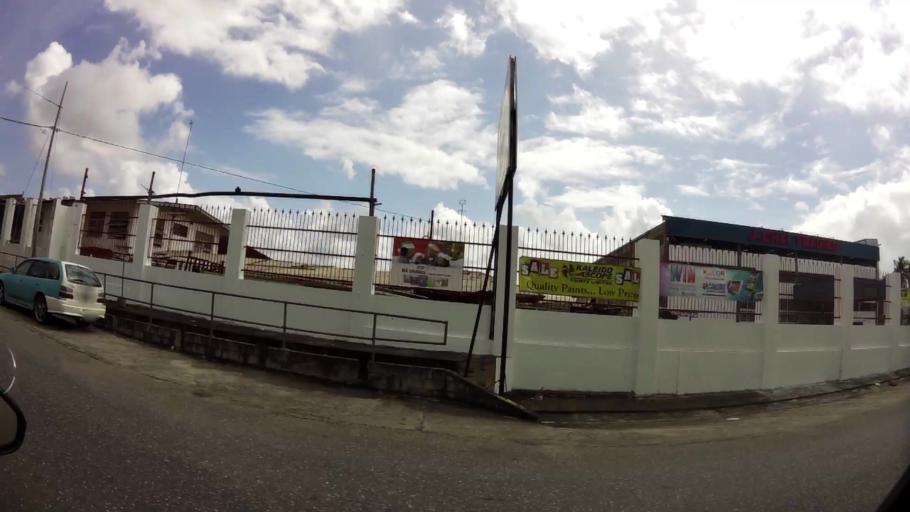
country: TT
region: Borough of Arima
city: Arima
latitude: 10.6359
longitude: -61.2897
